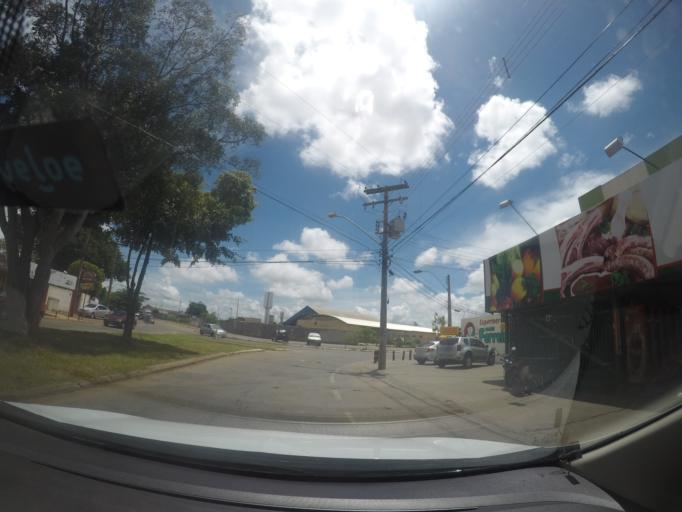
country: BR
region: Goias
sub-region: Goiania
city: Goiania
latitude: -16.6795
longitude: -49.3118
